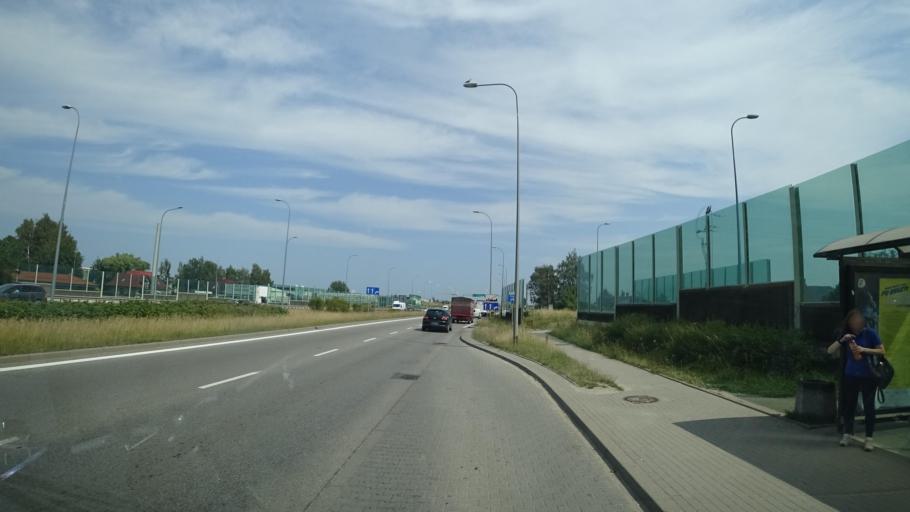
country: PL
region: Pomeranian Voivodeship
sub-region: Powiat gdanski
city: Kowale
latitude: 54.3497
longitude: 18.5123
